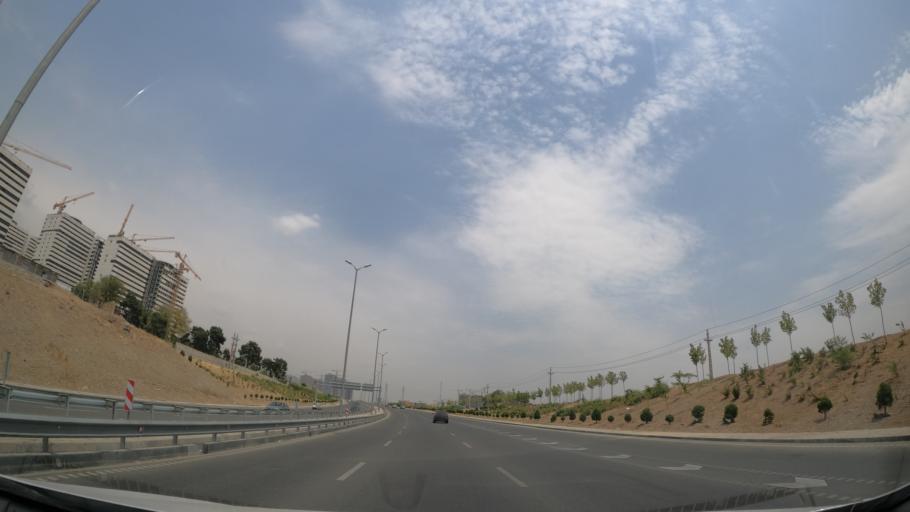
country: IR
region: Tehran
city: Shahr-e Qods
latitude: 35.7508
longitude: 51.1602
